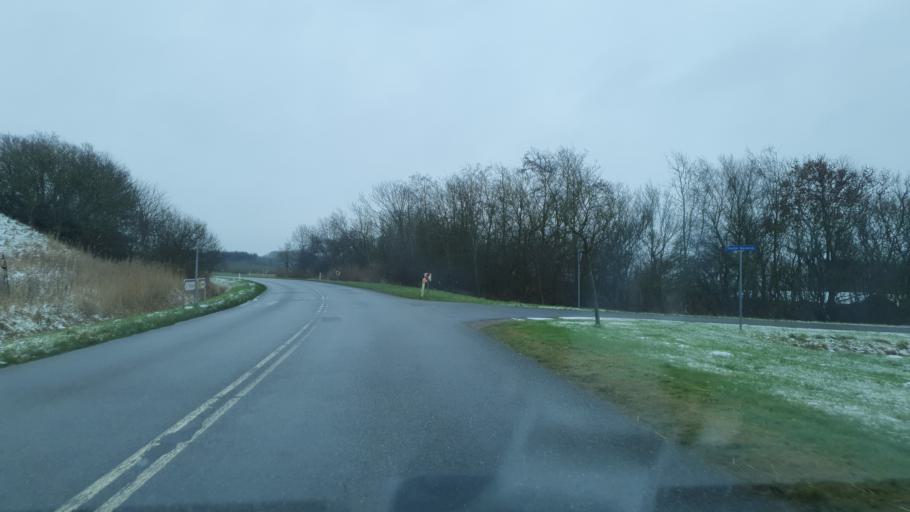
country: DK
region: North Denmark
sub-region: Jammerbugt Kommune
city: Brovst
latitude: 57.1025
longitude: 9.5035
